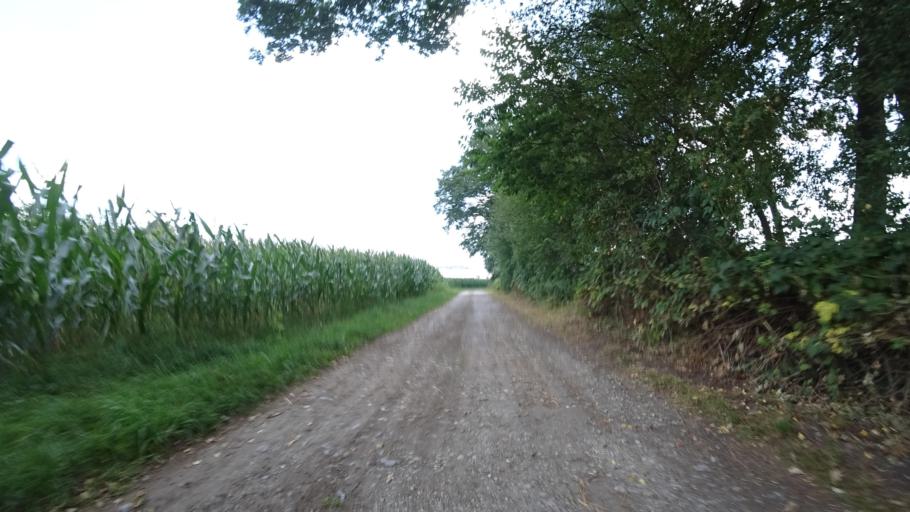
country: DE
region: North Rhine-Westphalia
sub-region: Regierungsbezirk Detmold
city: Guetersloh
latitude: 51.9246
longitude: 8.4190
